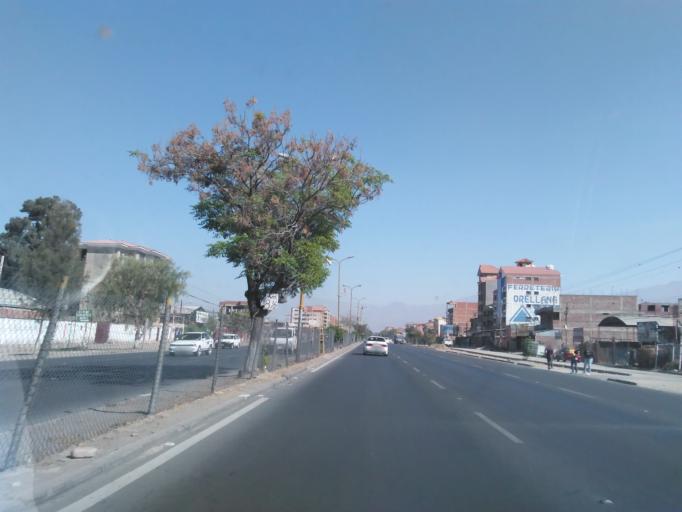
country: BO
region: Cochabamba
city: Cochabamba
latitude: -17.3911
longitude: -66.2342
